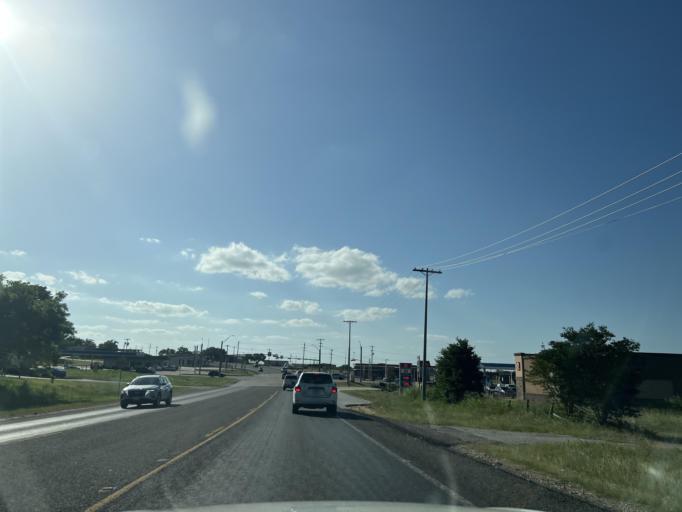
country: US
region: Texas
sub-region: Washington County
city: Brenham
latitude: 30.1772
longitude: -96.3838
